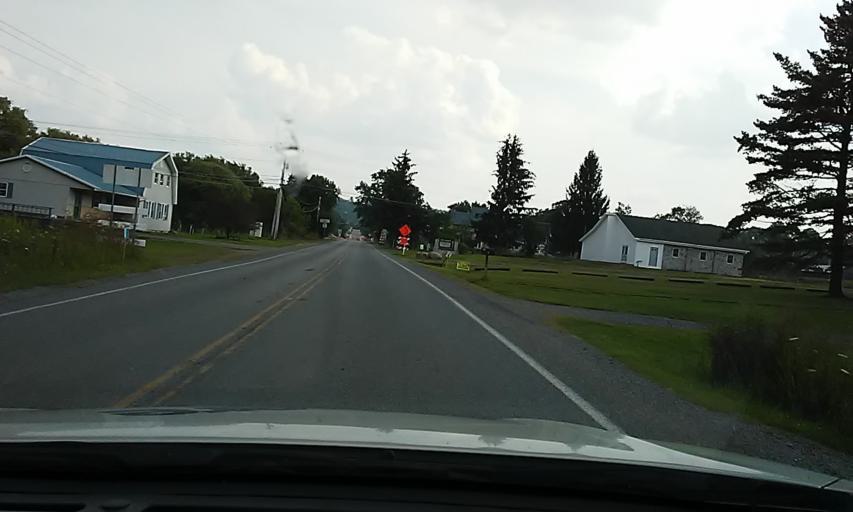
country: US
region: Pennsylvania
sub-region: Potter County
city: Coudersport
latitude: 41.8742
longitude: -77.8381
